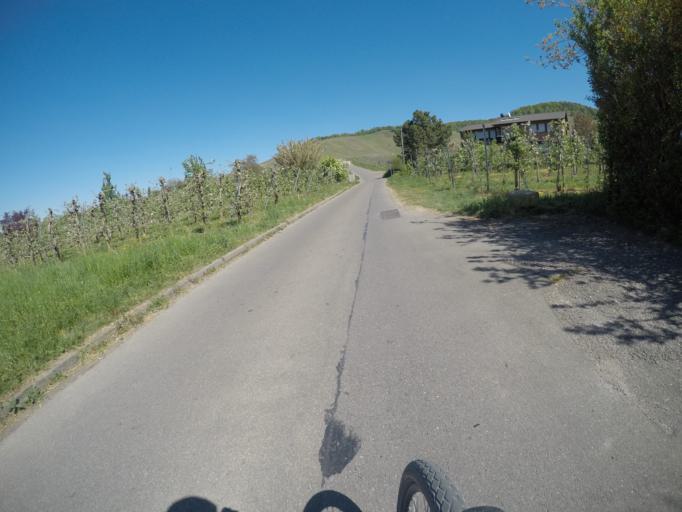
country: DE
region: Baden-Wuerttemberg
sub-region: Regierungsbezirk Stuttgart
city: Fellbach
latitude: 48.7889
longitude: 9.2727
